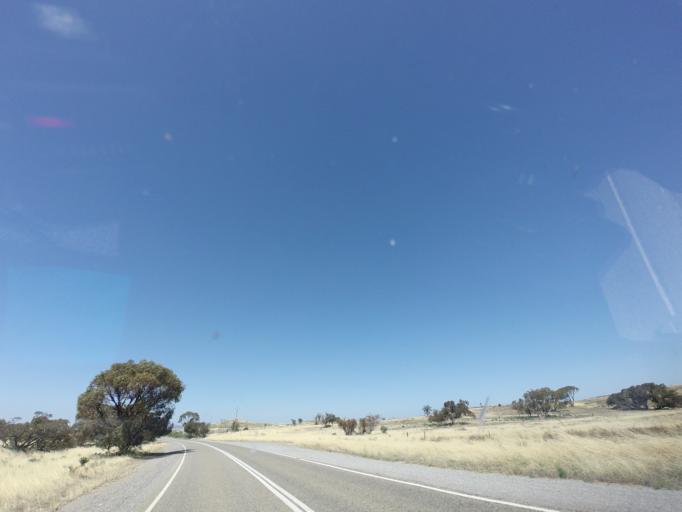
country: AU
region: South Australia
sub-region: Peterborough
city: Peterborough
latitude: -32.7342
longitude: 138.5907
